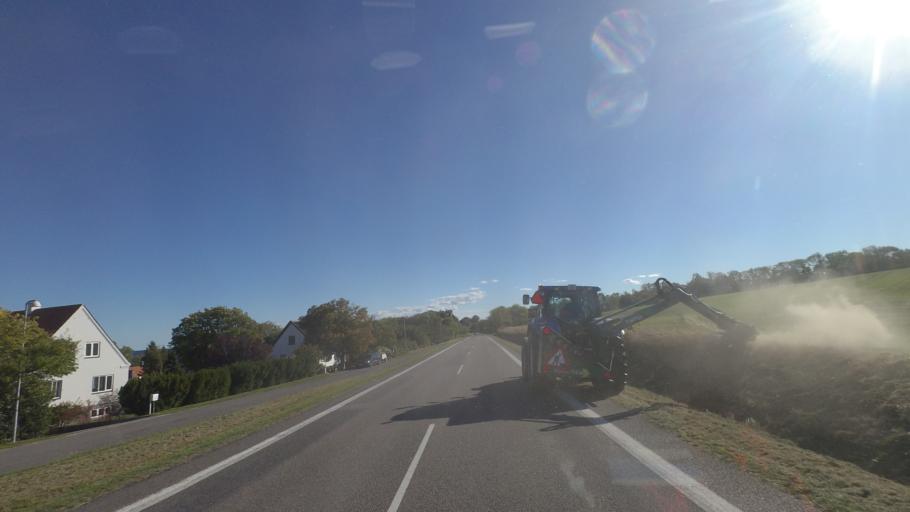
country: DK
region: Capital Region
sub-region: Bornholm Kommune
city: Nexo
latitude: 55.1016
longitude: 15.1443
